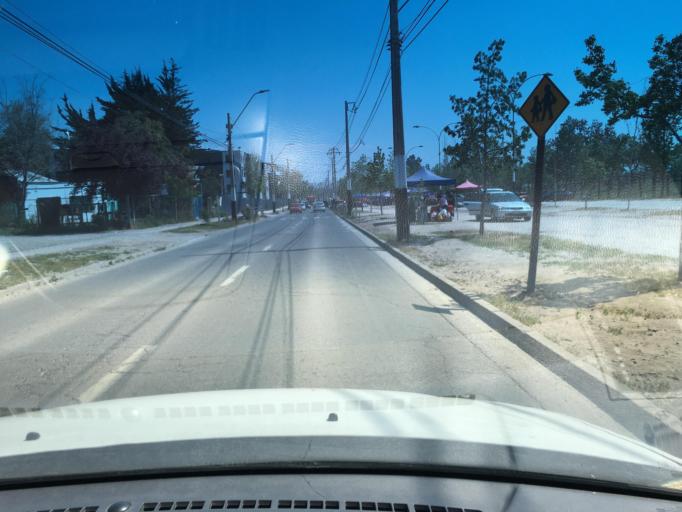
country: CL
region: Santiago Metropolitan
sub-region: Provincia de Santiago
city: Villa Presidente Frei, Nunoa, Santiago, Chile
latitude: -33.5167
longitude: -70.5524
